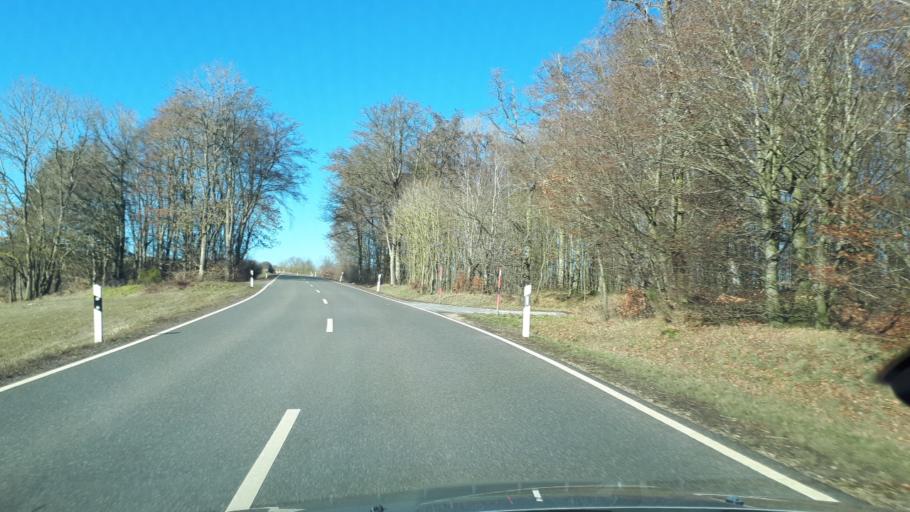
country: DE
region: Rheinland-Pfalz
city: Ellscheid
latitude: 50.1453
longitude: 6.9306
